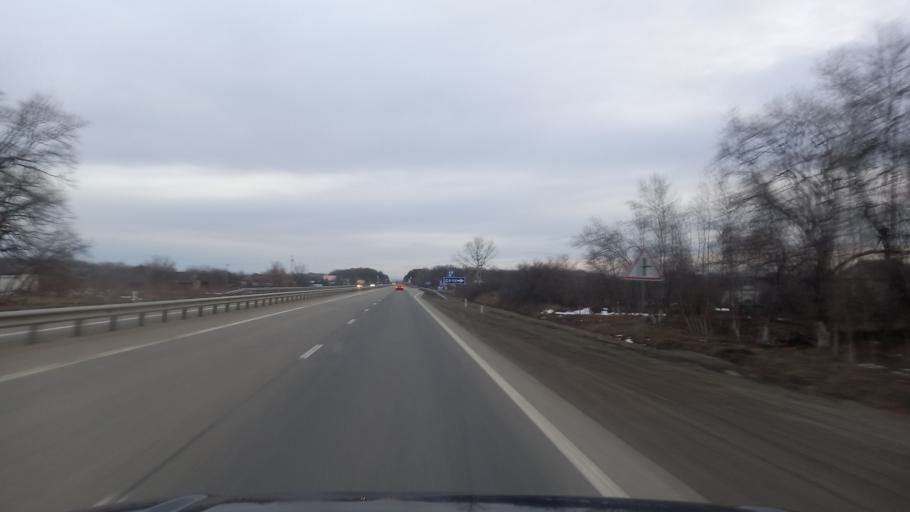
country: RU
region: Adygeya
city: Khanskaya
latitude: 44.7279
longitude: 39.9478
